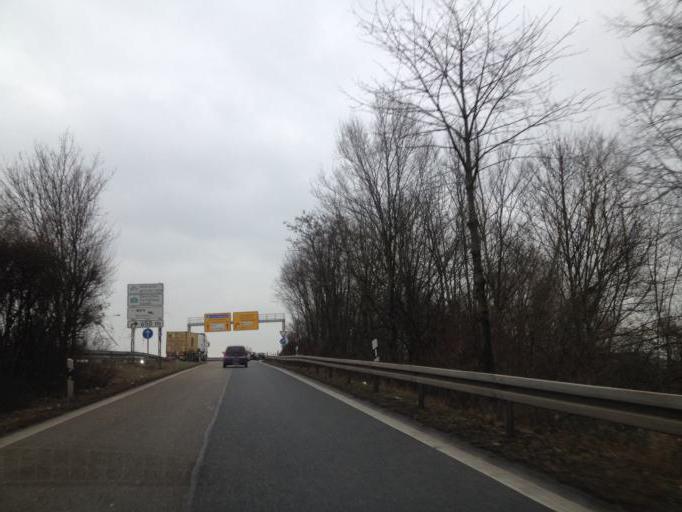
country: DE
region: Rheinland-Pfalz
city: Altrip
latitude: 49.4558
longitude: 8.5112
